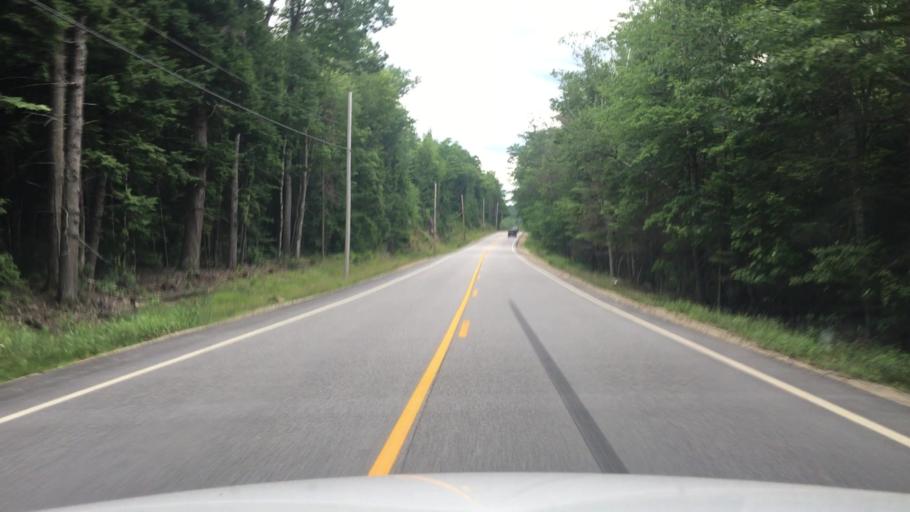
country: US
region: Maine
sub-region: Oxford County
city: Hartford
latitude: 44.3611
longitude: -70.3600
